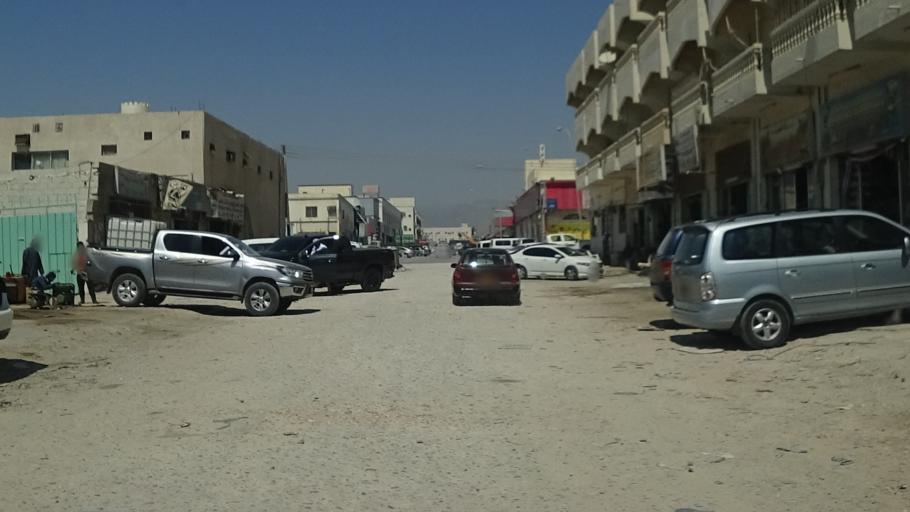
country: OM
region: Zufar
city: Salalah
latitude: 17.0192
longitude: 54.0555
